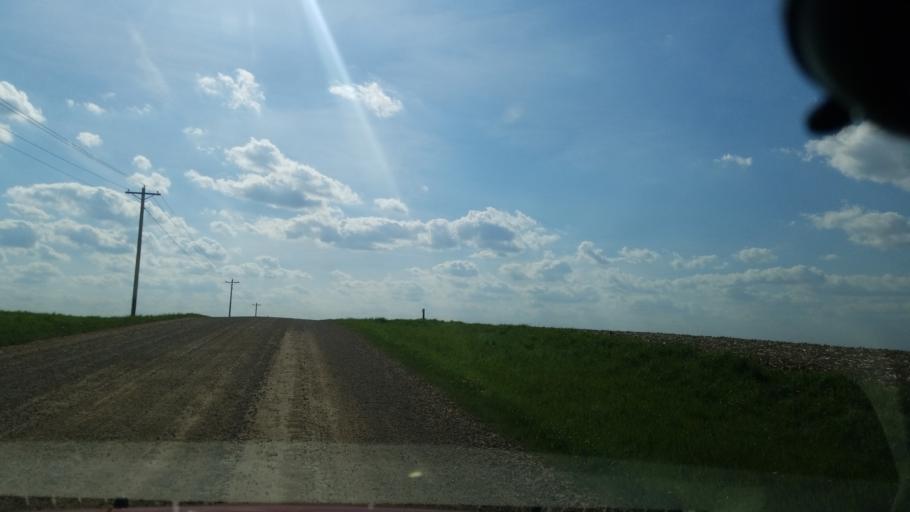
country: US
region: Iowa
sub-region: Jackson County
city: Maquoketa
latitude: 42.2150
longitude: -90.7204
